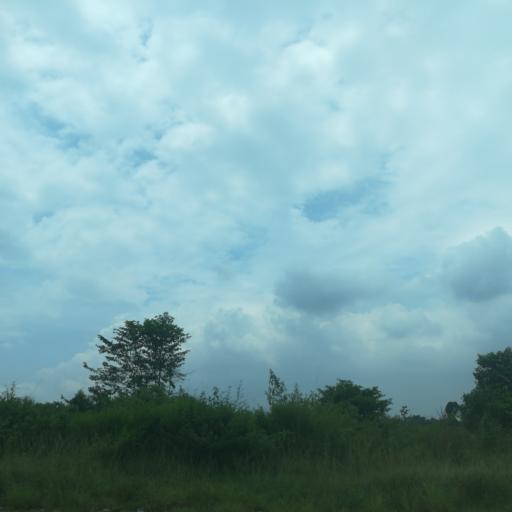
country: NG
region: Lagos
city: Ejirin
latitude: 6.6653
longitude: 3.7931
